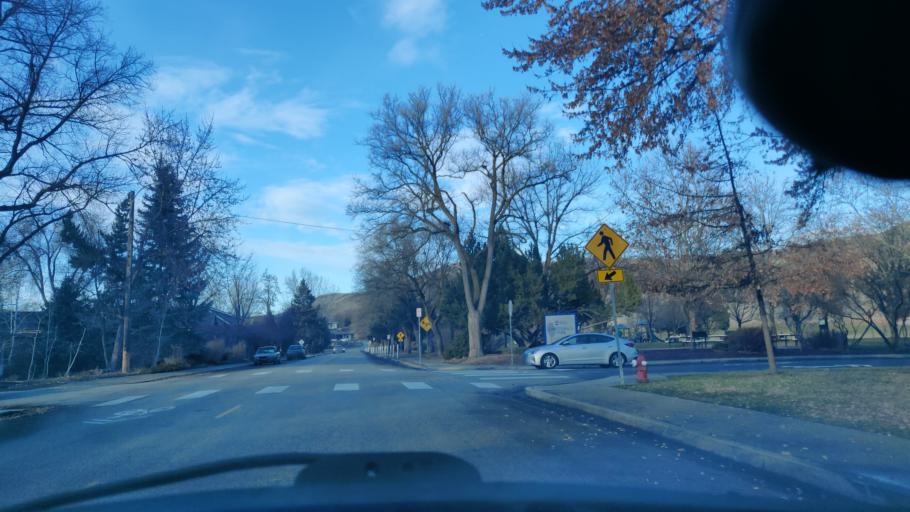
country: US
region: Idaho
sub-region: Ada County
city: Boise
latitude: 43.6335
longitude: -116.2034
